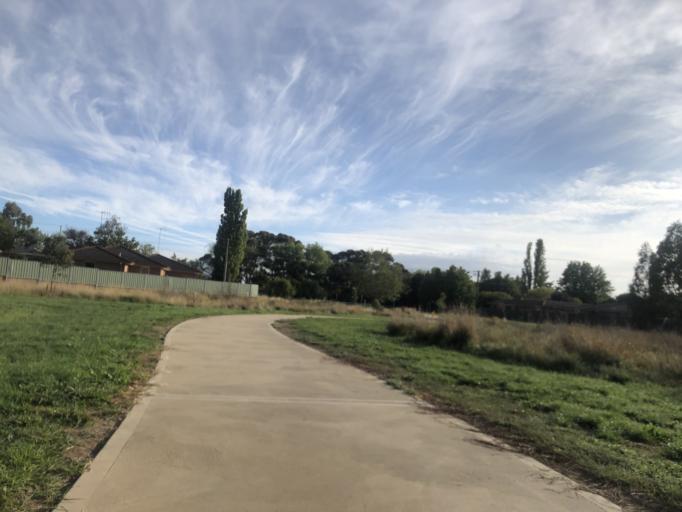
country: AU
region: New South Wales
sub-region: Orange Municipality
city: Orange
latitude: -33.2946
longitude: 149.0927
